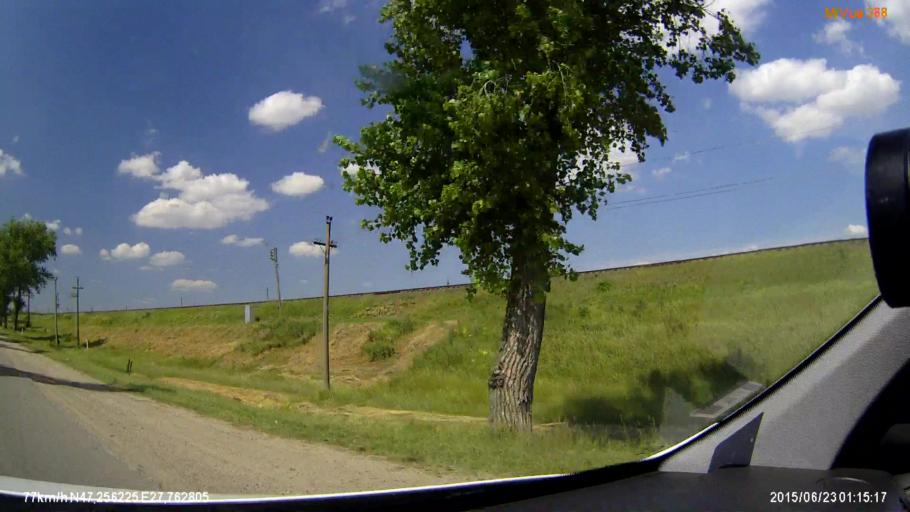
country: RO
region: Iasi
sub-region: Comuna Ungheni
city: Bosia
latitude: 47.2560
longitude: 27.7629
